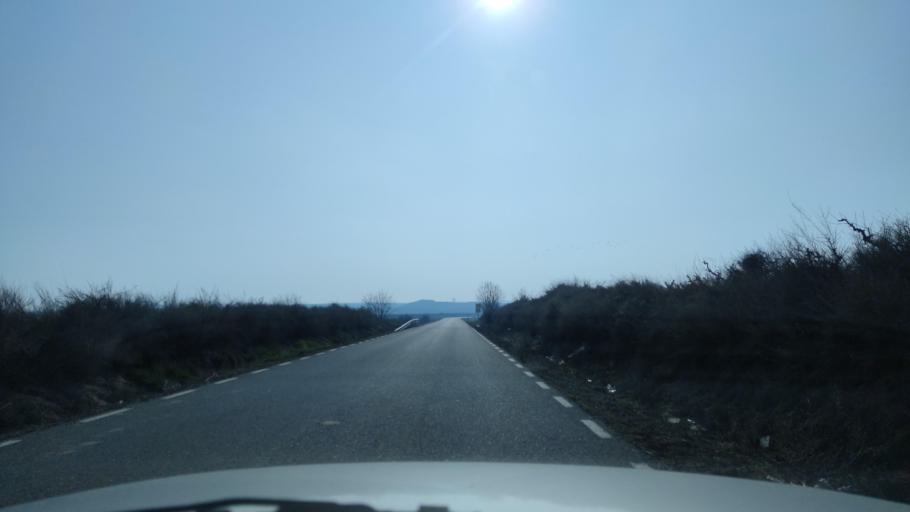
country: ES
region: Catalonia
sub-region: Provincia de Lleida
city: Sunyer
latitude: 41.5382
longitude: 0.5770
